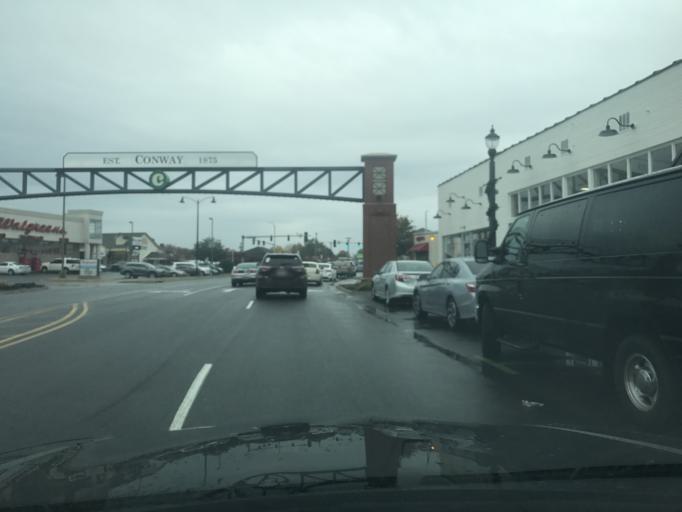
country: US
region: Arkansas
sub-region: Faulkner County
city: Conway
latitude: 35.0915
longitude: -92.4380
